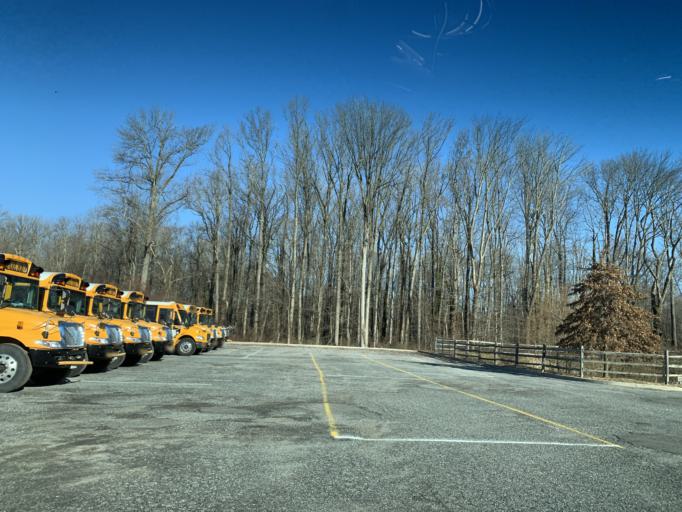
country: US
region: Maryland
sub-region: Harford County
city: Aberdeen
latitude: 39.5676
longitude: -76.2000
